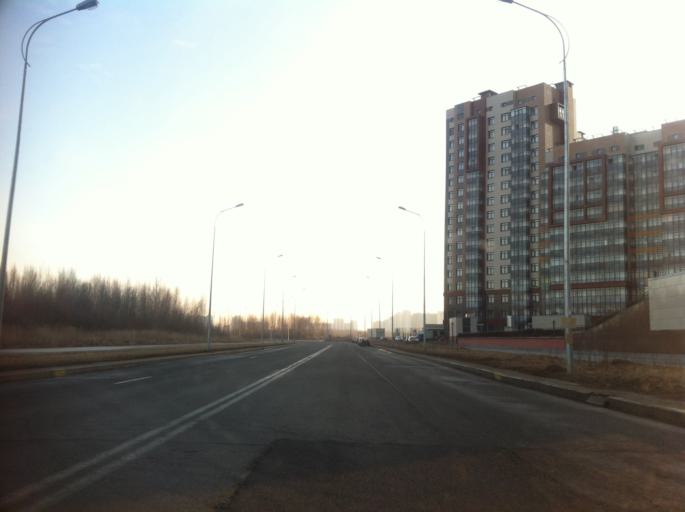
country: RU
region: St.-Petersburg
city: Sosnovaya Polyana
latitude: 59.8529
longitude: 30.1378
